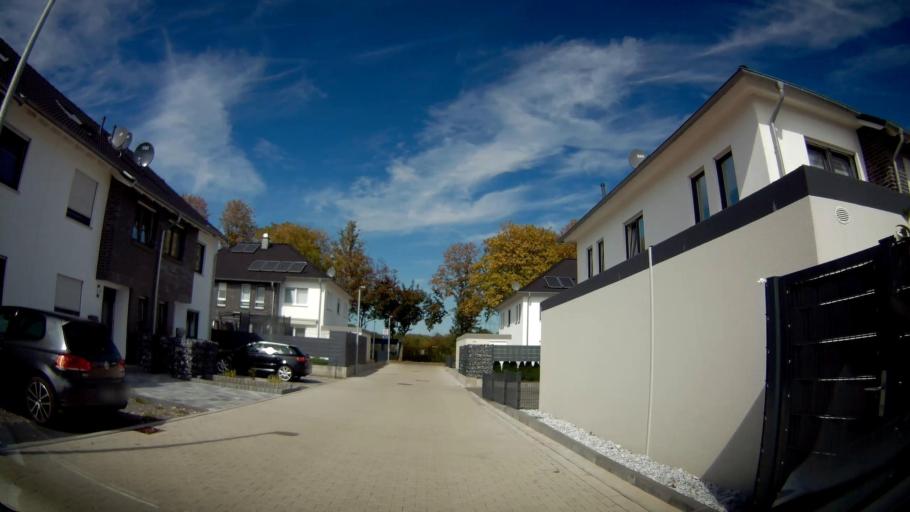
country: DE
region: North Rhine-Westphalia
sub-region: Regierungsbezirk Munster
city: Gladbeck
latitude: 51.5484
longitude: 7.0325
